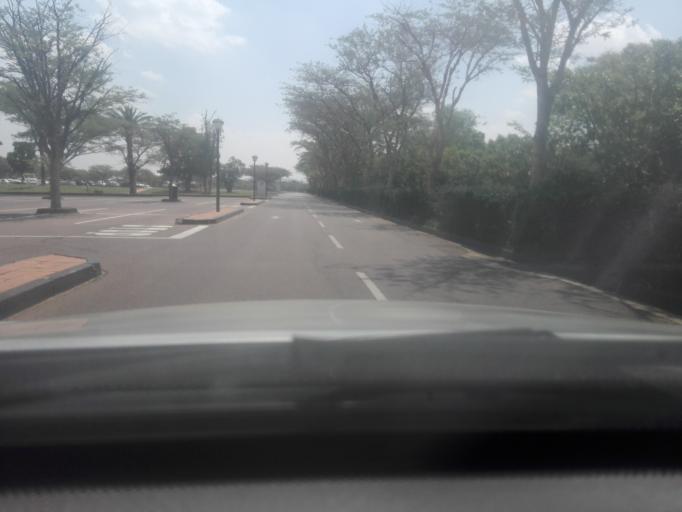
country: BW
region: Kweneng
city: Mogoditshane
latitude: -24.6389
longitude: 25.8782
